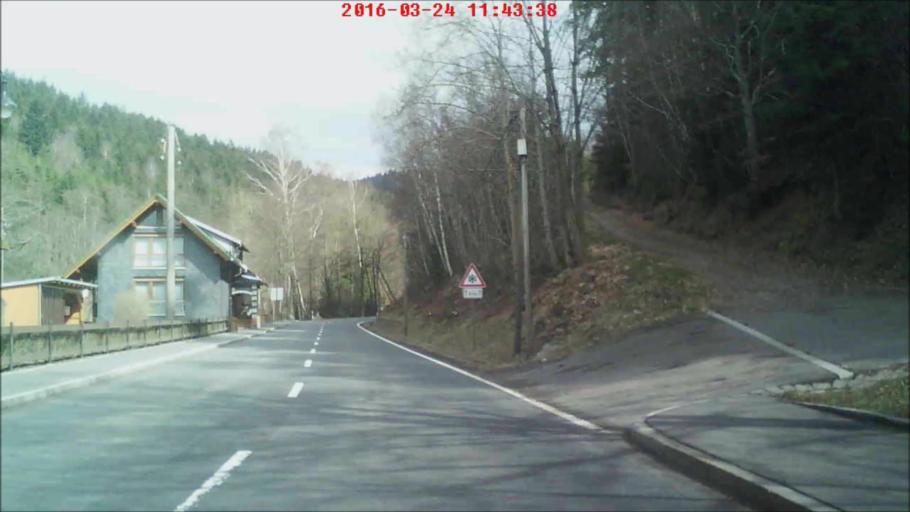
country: DE
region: Thuringia
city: Bachfeld
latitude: 50.4509
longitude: 10.9737
